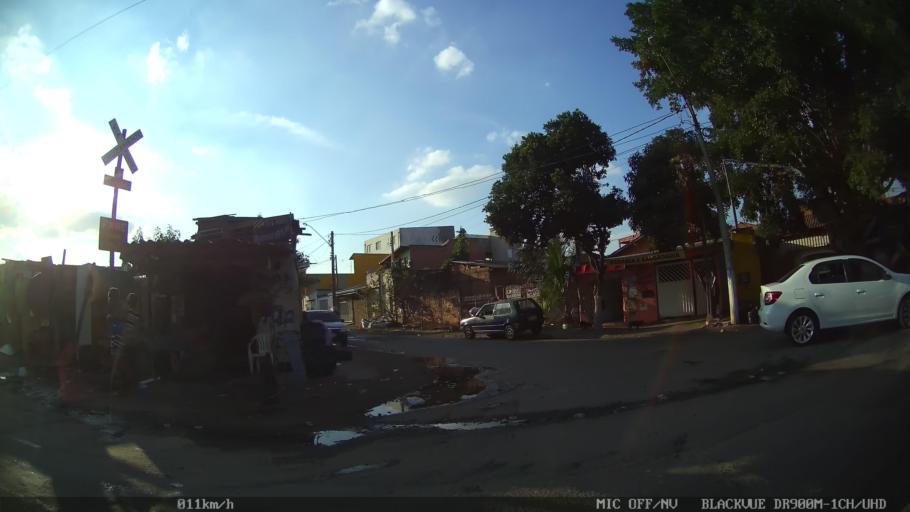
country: BR
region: Sao Paulo
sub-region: Hortolandia
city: Hortolandia
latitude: -22.8598
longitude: -47.1586
